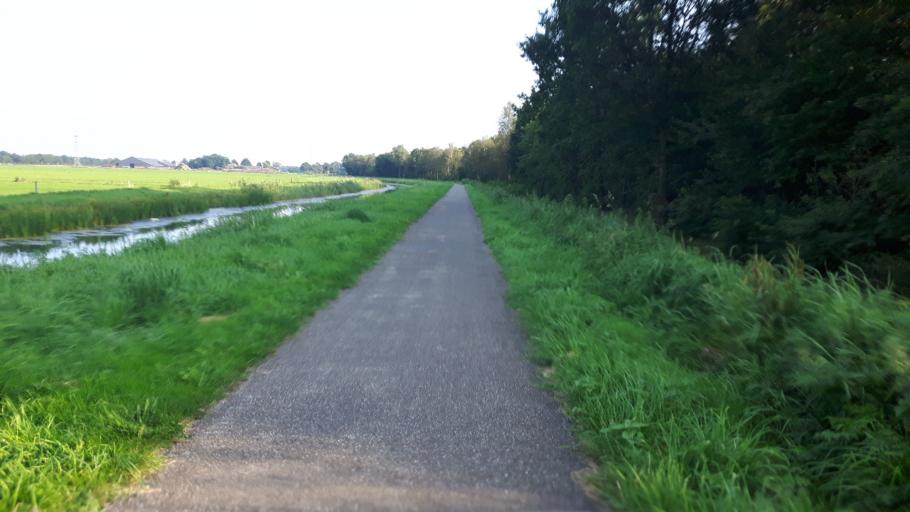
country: NL
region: Drenthe
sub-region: Gemeente Tynaarlo
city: Vries
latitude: 53.1234
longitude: 6.4985
